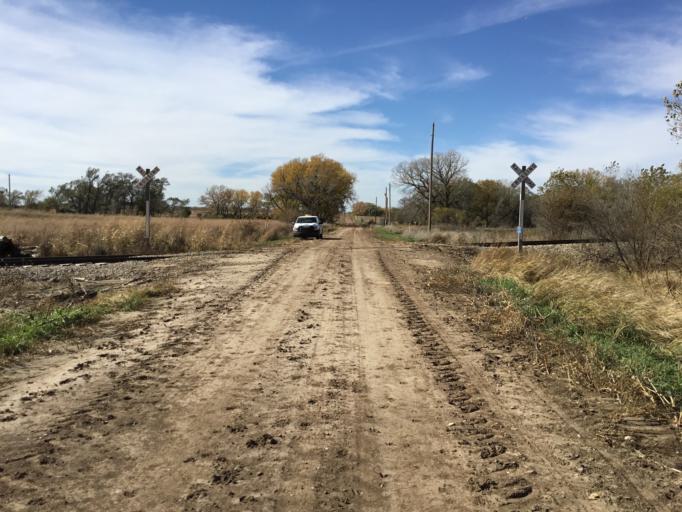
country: US
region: Kansas
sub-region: Lincoln County
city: Lincoln
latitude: 38.9148
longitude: -98.0018
